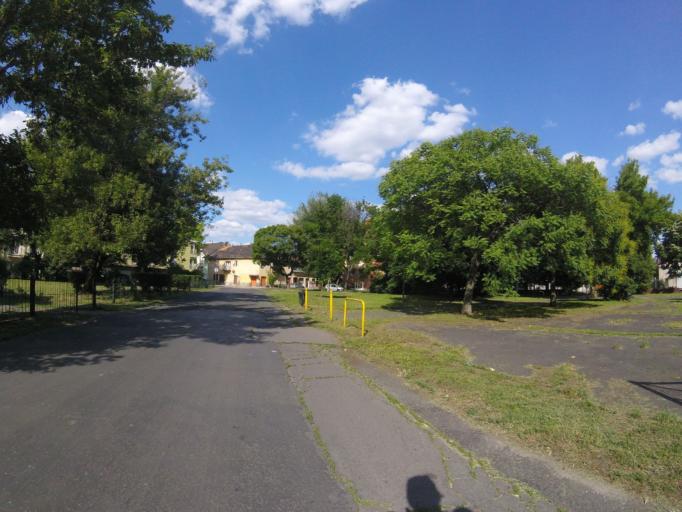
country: HU
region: Budapest
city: Budapest IV. keruelet
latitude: 47.5524
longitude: 19.0946
